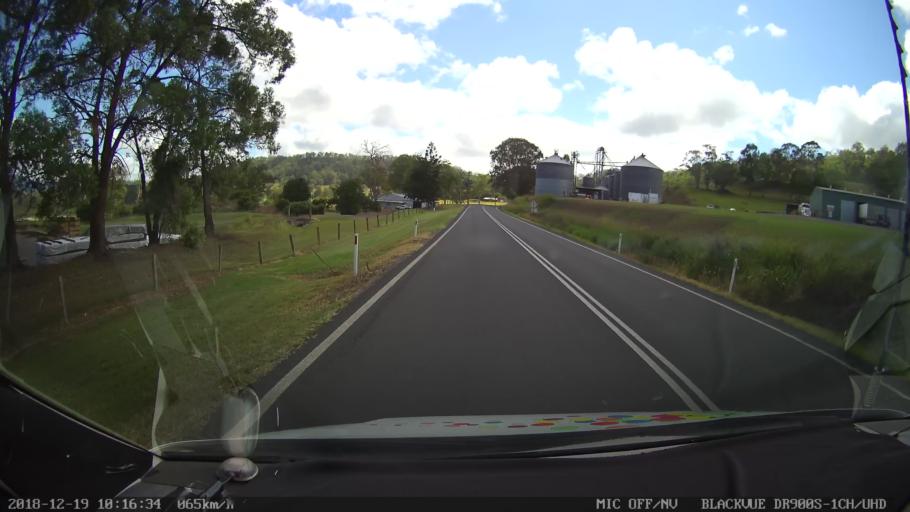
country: AU
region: New South Wales
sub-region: Kyogle
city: Kyogle
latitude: -28.6071
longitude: 153.0228
